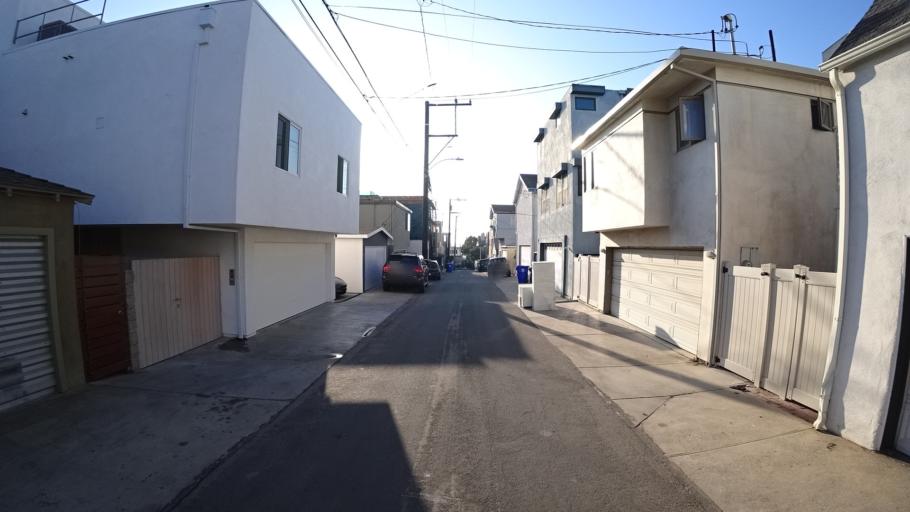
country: US
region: California
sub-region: Los Angeles County
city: Manhattan Beach
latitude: 33.9001
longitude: -118.4147
